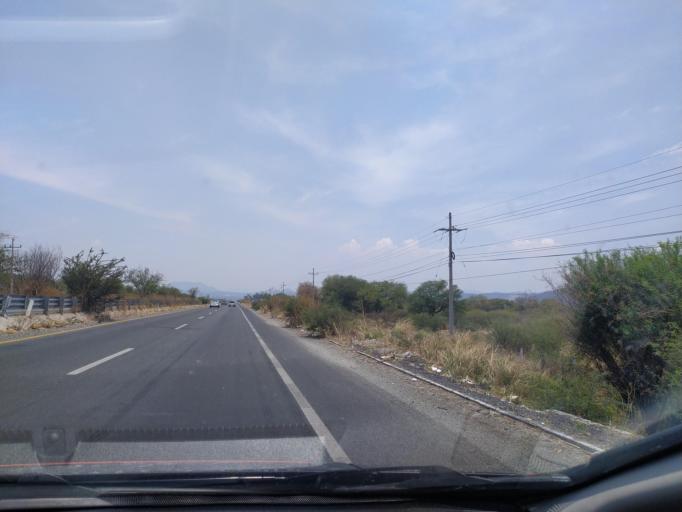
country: MX
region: Jalisco
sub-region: Acatlan de Juarez
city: Villa de los Ninos
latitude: 20.3593
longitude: -103.5917
